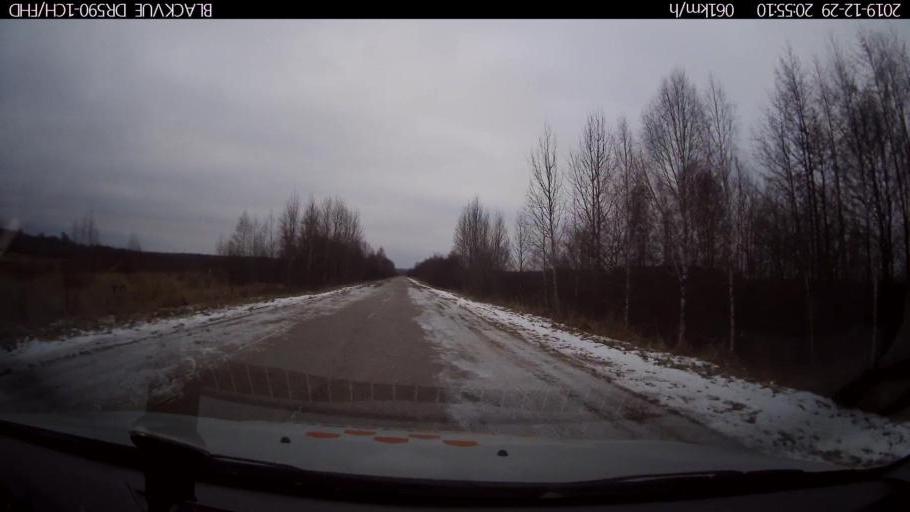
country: RU
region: Nizjnij Novgorod
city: Afonino
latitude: 56.1586
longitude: 43.9934
